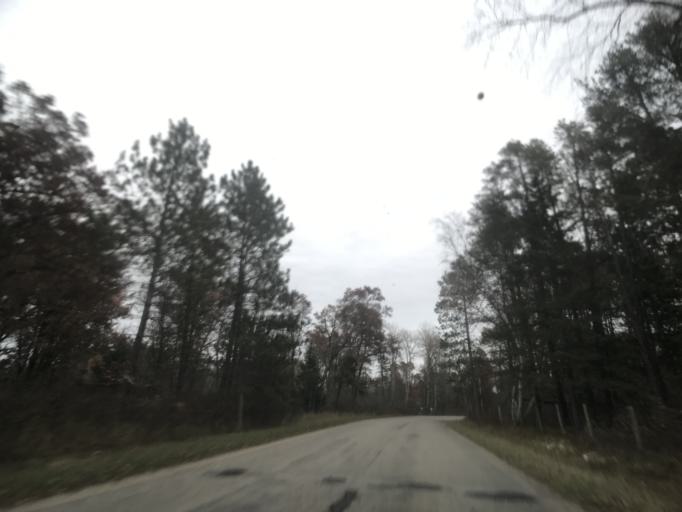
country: US
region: Wisconsin
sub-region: Oconto County
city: Gillett
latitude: 45.3313
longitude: -88.2796
